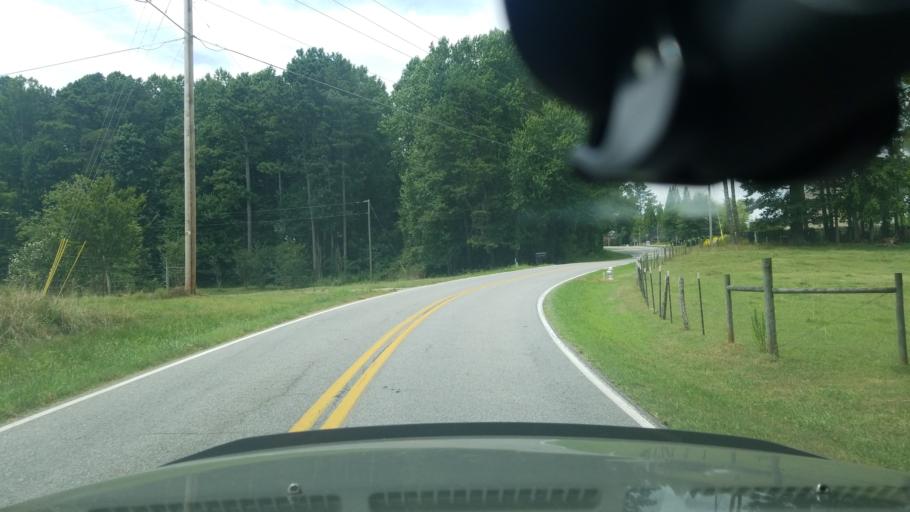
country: US
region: Georgia
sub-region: Forsyth County
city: Cumming
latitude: 34.2253
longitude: -84.2128
